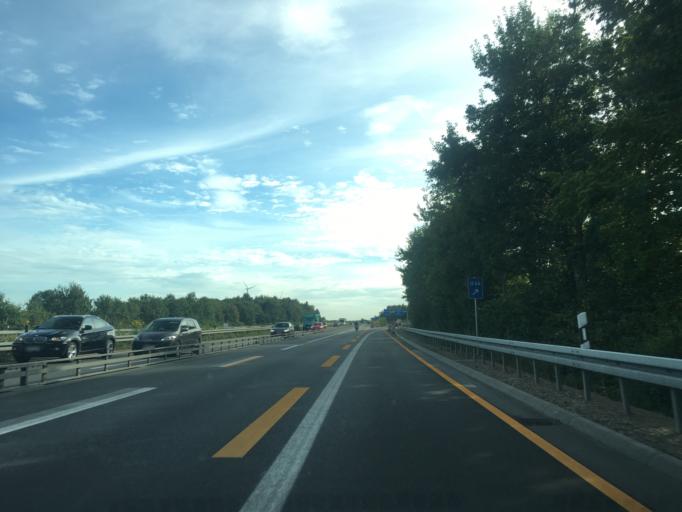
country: DE
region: North Rhine-Westphalia
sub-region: Regierungsbezirk Munster
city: Haltern
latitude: 51.7103
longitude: 7.1496
